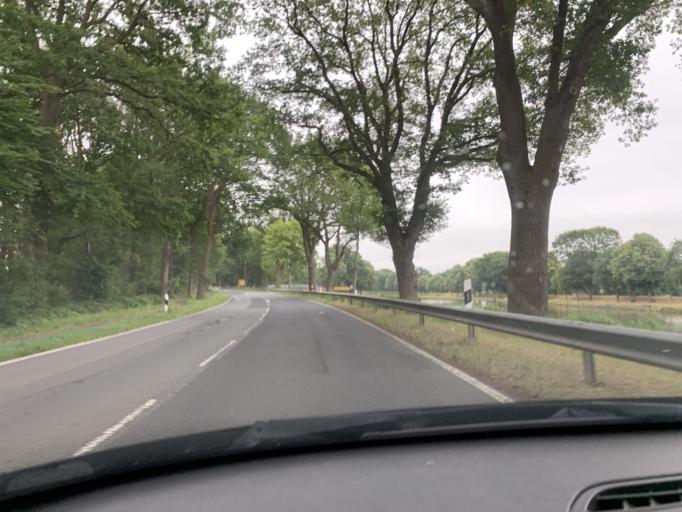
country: DE
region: Lower Saxony
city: Lingen
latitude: 52.4843
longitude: 7.2974
